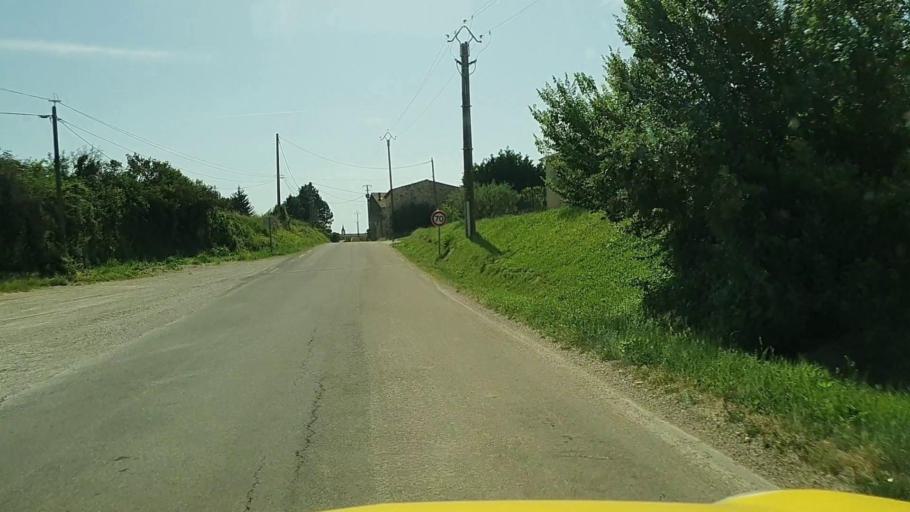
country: FR
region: Languedoc-Roussillon
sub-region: Departement du Gard
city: Sabran
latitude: 44.1163
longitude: 4.5135
